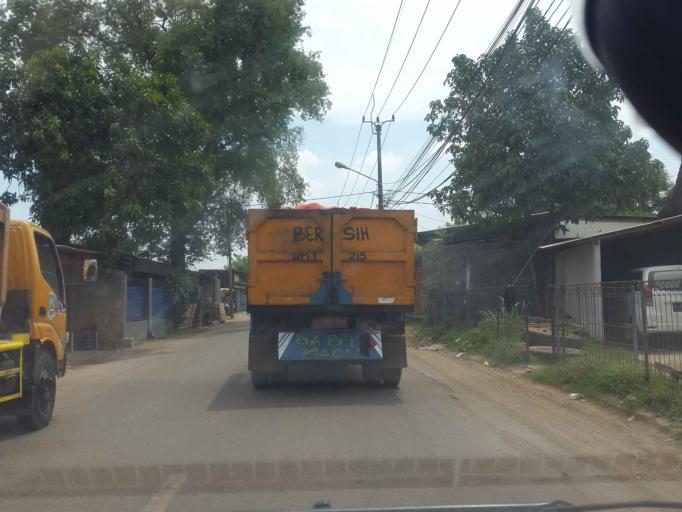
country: ID
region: Banten
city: Tangerang
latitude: -6.1443
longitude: 106.6188
